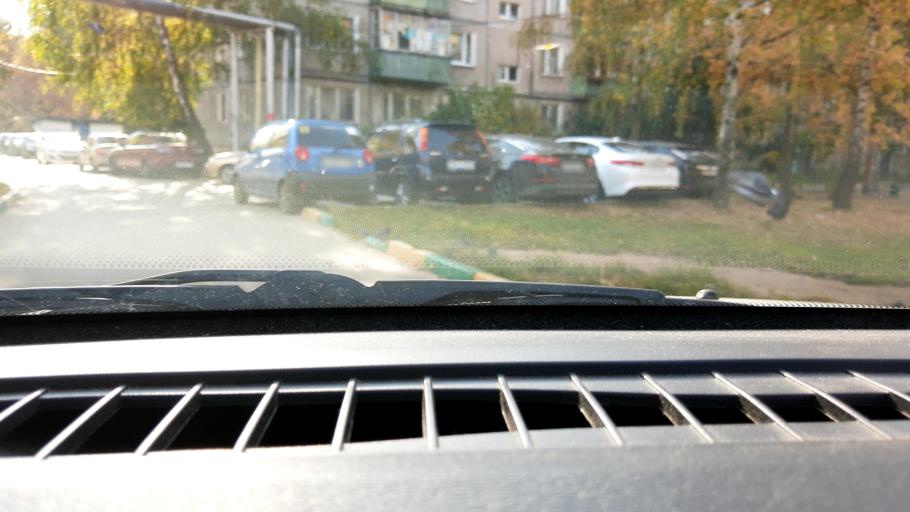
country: RU
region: Nizjnij Novgorod
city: Nizhniy Novgorod
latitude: 56.2584
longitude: 43.9205
